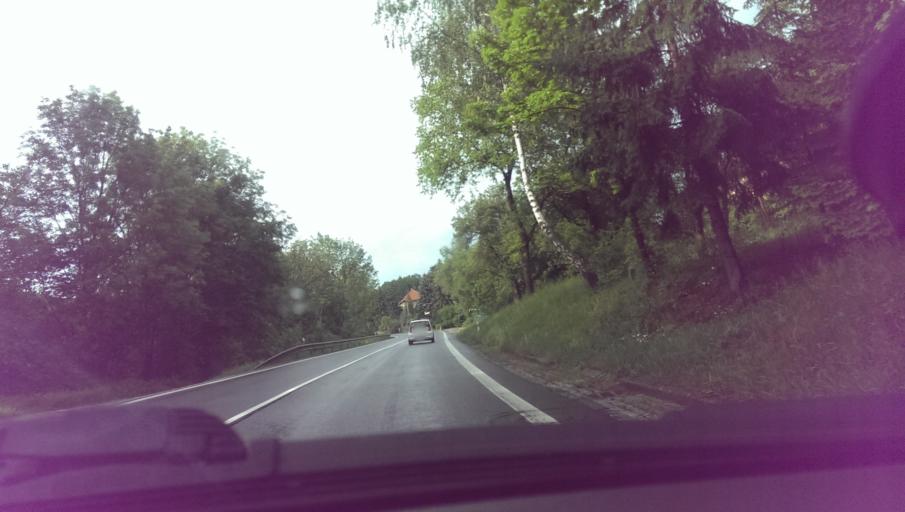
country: CZ
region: Zlin
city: Breznice
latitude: 49.1910
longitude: 17.6567
